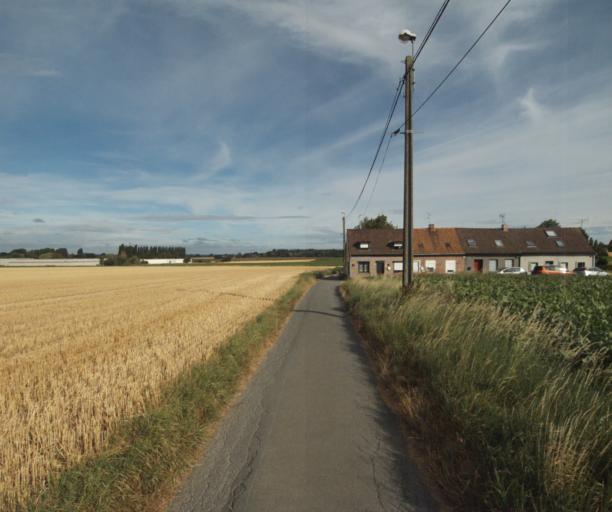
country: FR
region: Nord-Pas-de-Calais
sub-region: Departement du Nord
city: Linselles
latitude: 50.7415
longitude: 3.0758
